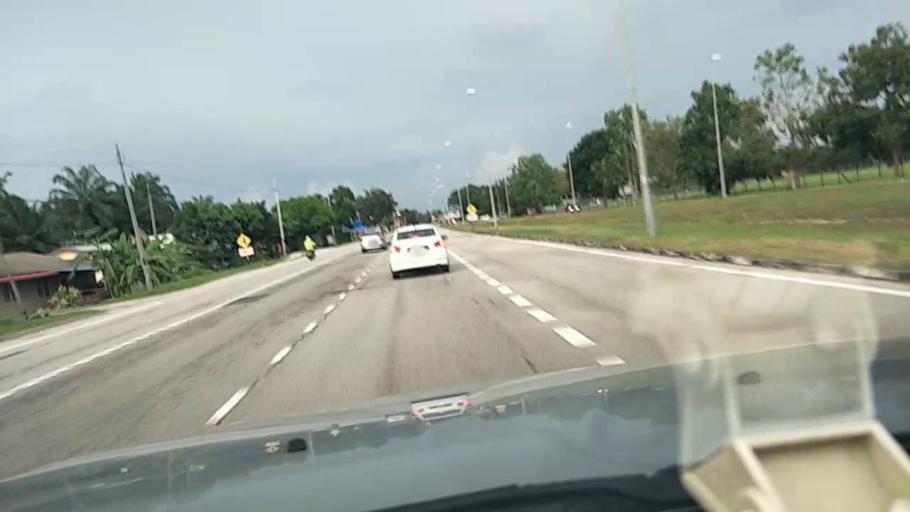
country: MY
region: Perak
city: Kampong Dungun
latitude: 3.1257
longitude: 101.3706
